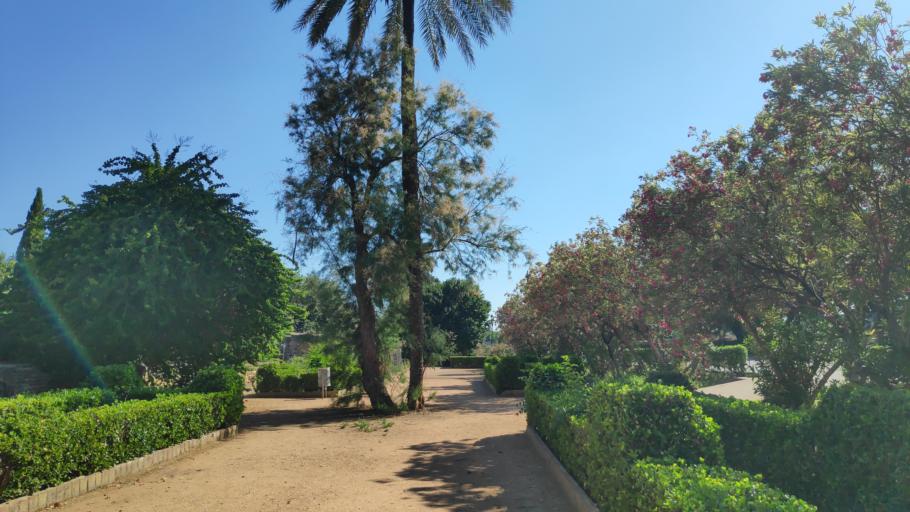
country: ES
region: Andalusia
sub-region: Province of Cordoba
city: Cordoba
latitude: 37.8758
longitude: -4.7813
